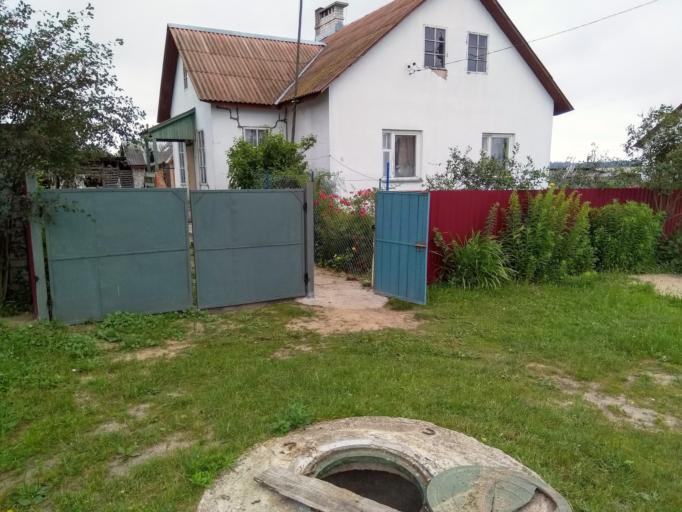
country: BY
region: Mogilev
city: Myazhysyatki
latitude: 53.7741
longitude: 30.0099
